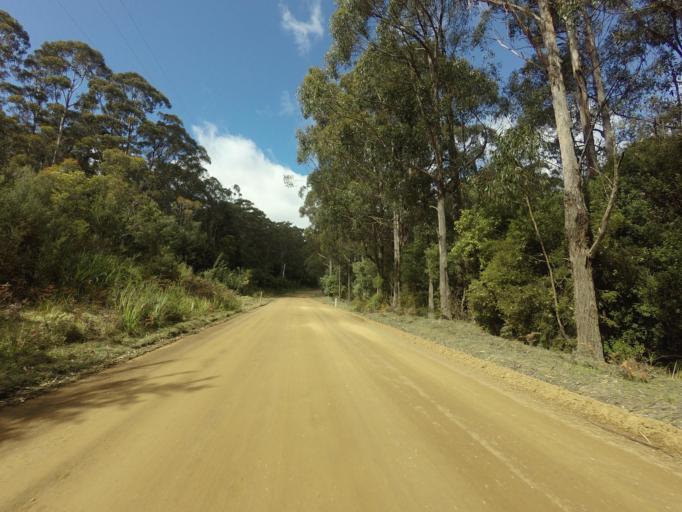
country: AU
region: Tasmania
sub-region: Huon Valley
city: Geeveston
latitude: -43.4145
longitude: 146.9062
